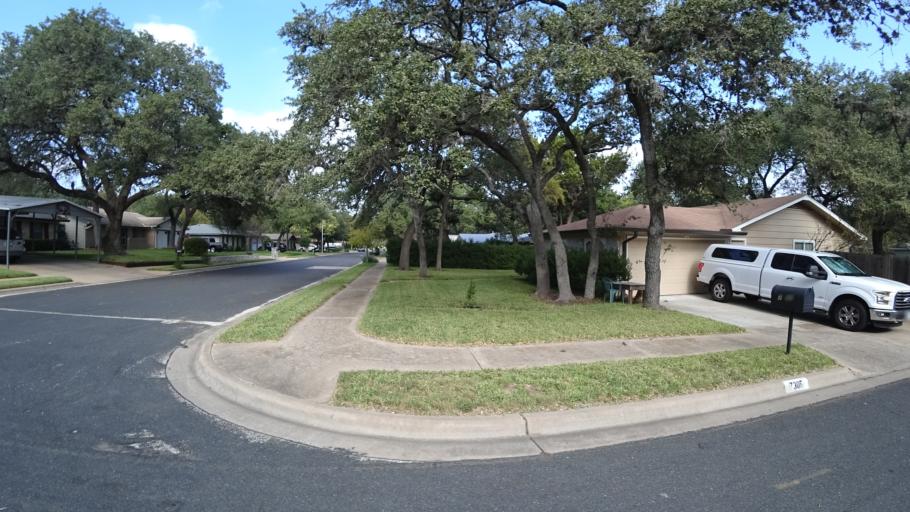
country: US
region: Texas
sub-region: Travis County
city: Shady Hollow
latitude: 30.2006
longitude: -97.8133
